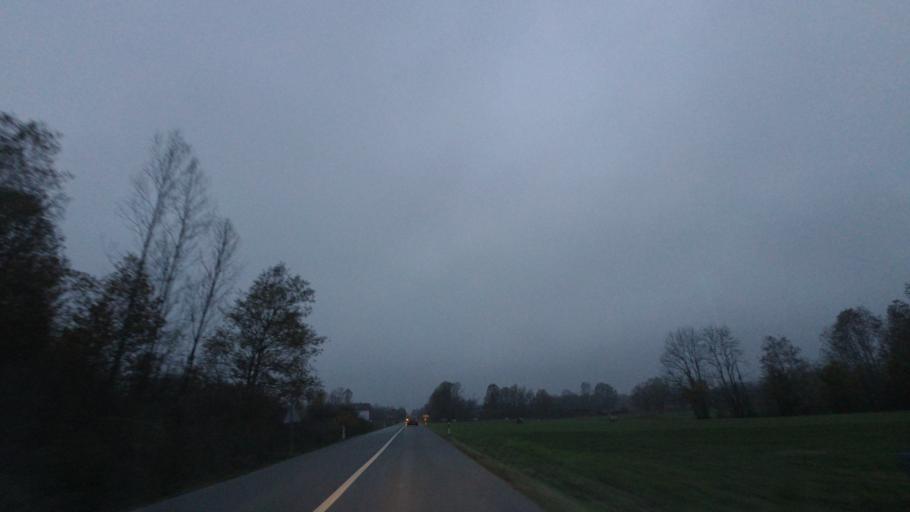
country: HR
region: Sisacko-Moslavacka
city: Glina
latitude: 45.3747
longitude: 16.1376
